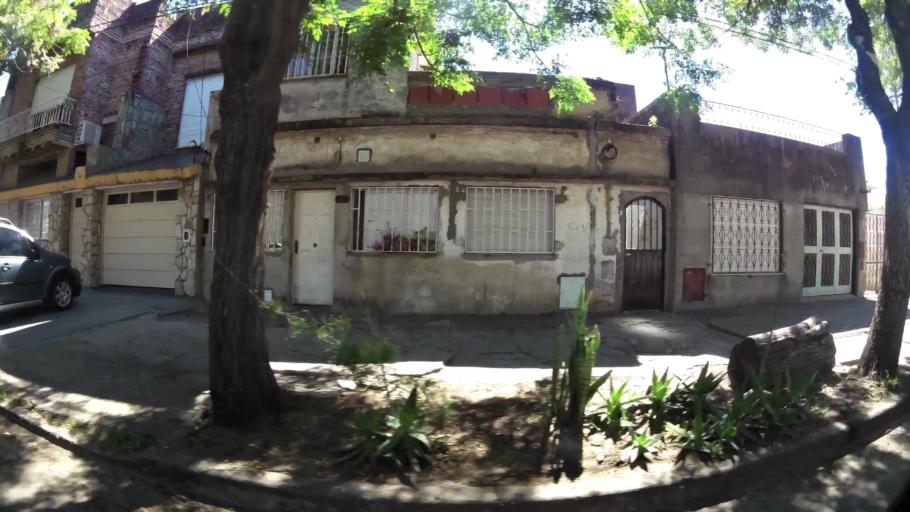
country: AR
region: Santa Fe
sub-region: Departamento de Rosario
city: Rosario
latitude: -32.9375
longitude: -60.6987
